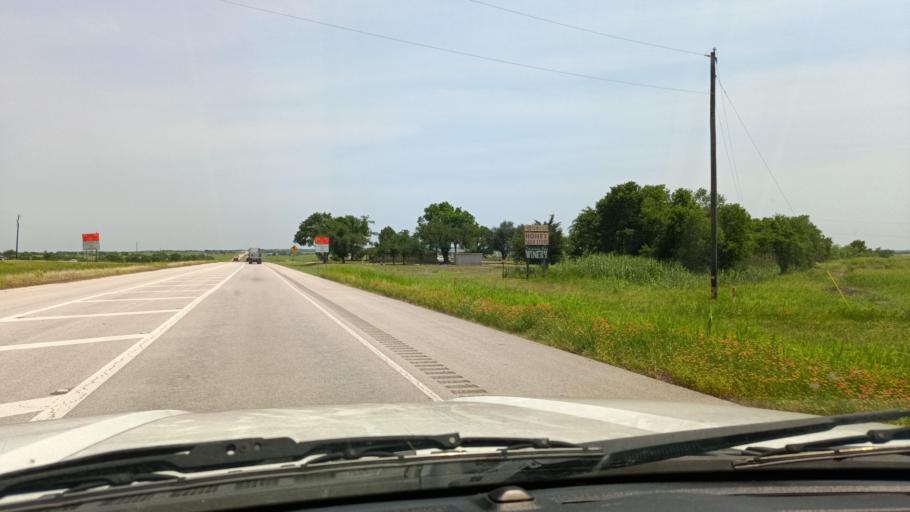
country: US
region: Texas
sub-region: Bell County
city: Little River-Academy
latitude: 30.9955
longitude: -97.2865
